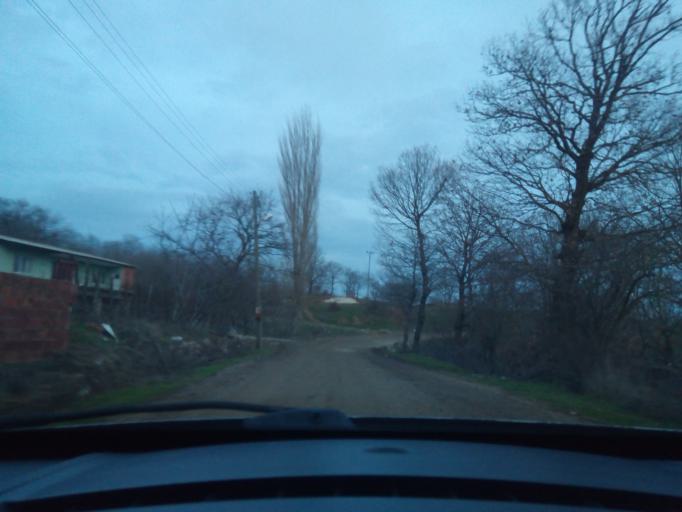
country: TR
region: Balikesir
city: Omerkoy
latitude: 39.9105
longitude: 28.0392
